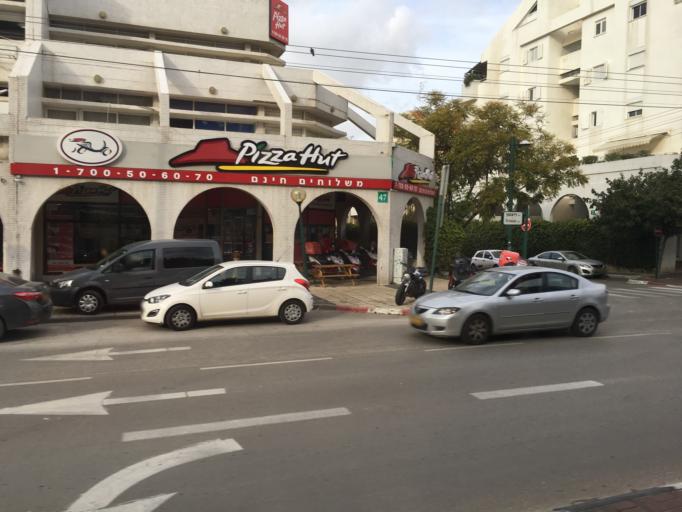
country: IL
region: Central District
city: Kfar Saba
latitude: 32.1770
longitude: 34.9009
